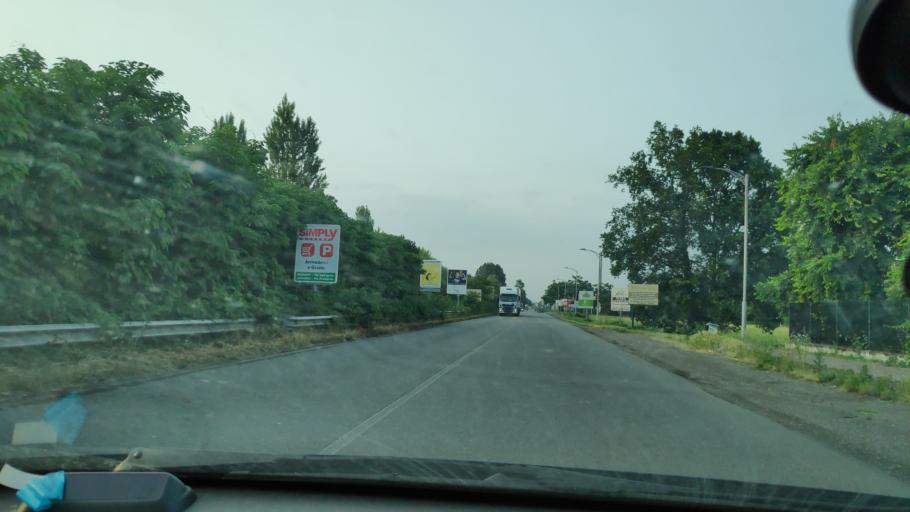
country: IT
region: Lombardy
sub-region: Citta metropolitana di Milano
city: Rozzano
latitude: 45.3824
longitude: 9.1444
